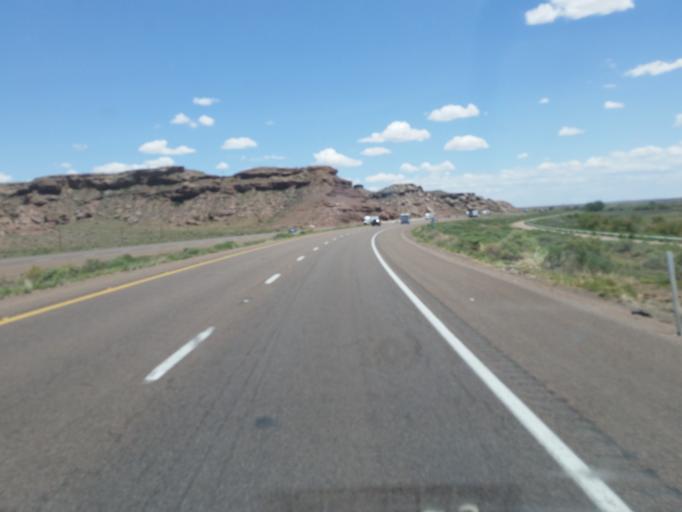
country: US
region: Arizona
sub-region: Navajo County
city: Joseph City
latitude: 34.9402
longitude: -110.2815
